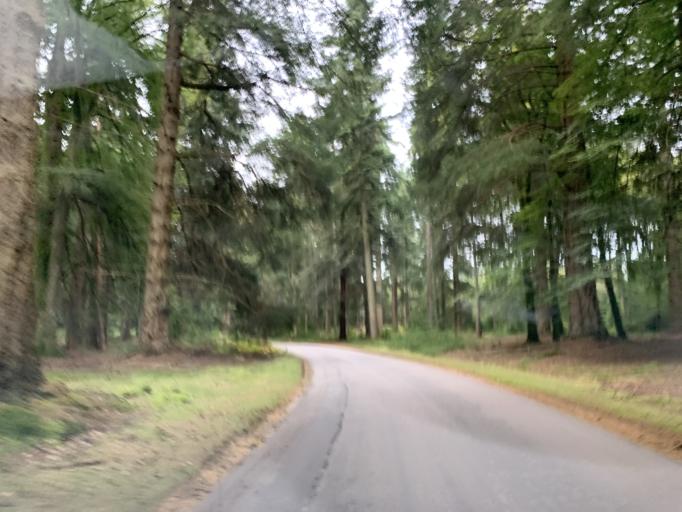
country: GB
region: England
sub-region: Hampshire
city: Lyndhurst
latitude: 50.8481
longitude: -1.6237
